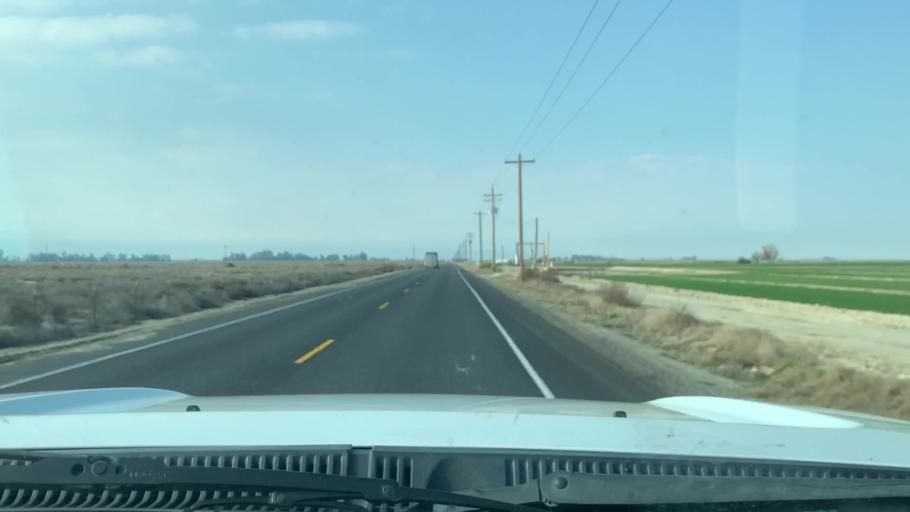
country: US
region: California
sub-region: Kern County
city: Buttonwillow
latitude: 35.4421
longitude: -119.3795
